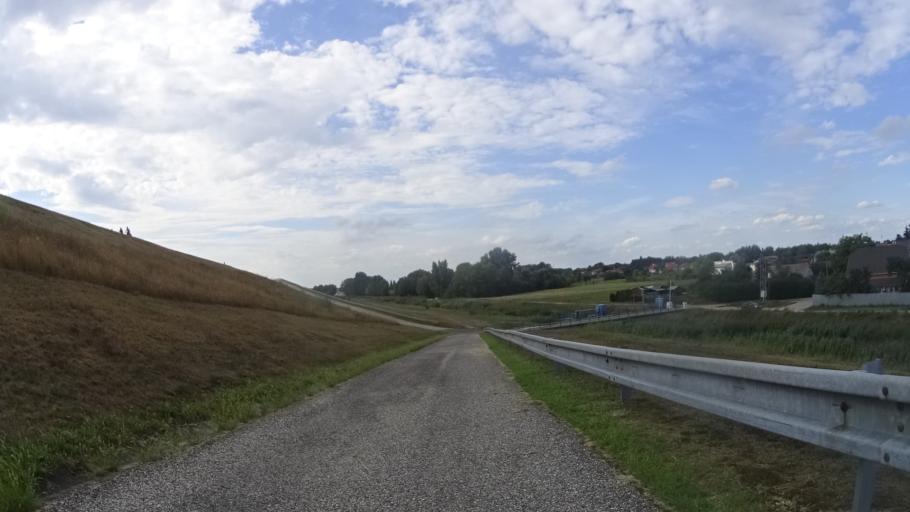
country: SK
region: Trnavsky
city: Gabcikovo
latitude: 47.8978
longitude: 17.5247
